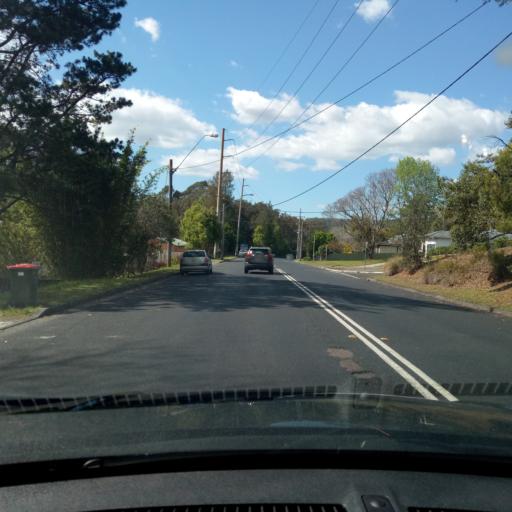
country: AU
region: New South Wales
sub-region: Gosford Shire
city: Narara
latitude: -33.4029
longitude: 151.3451
